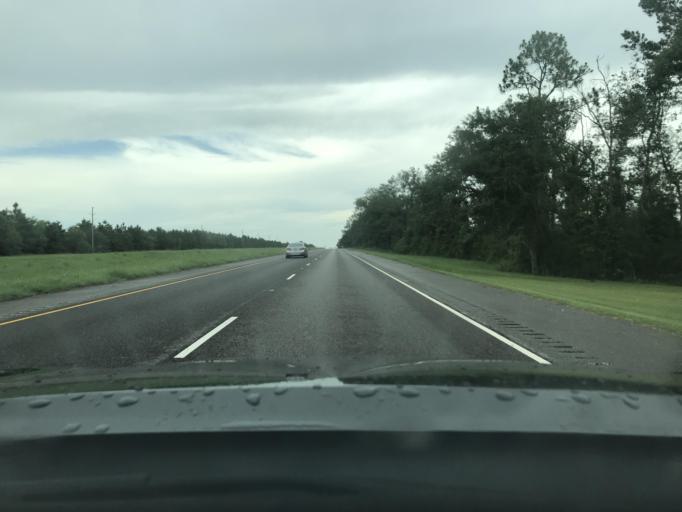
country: US
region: Louisiana
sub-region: Calcasieu Parish
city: Moss Bluff
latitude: 30.3926
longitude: -93.2250
